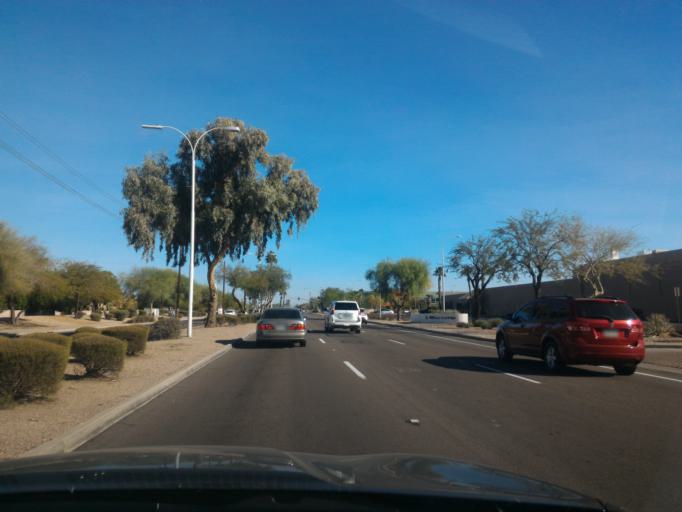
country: US
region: Arizona
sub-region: Maricopa County
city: Chandler
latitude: 33.3059
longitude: -111.8834
